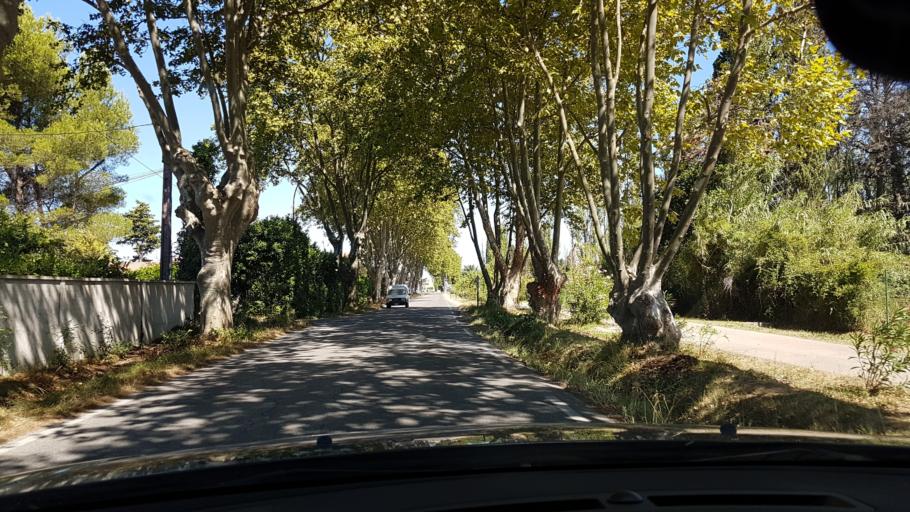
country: FR
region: Provence-Alpes-Cote d'Azur
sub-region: Departement des Bouches-du-Rhone
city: Saint-Andiol
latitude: 43.8276
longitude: 4.9452
